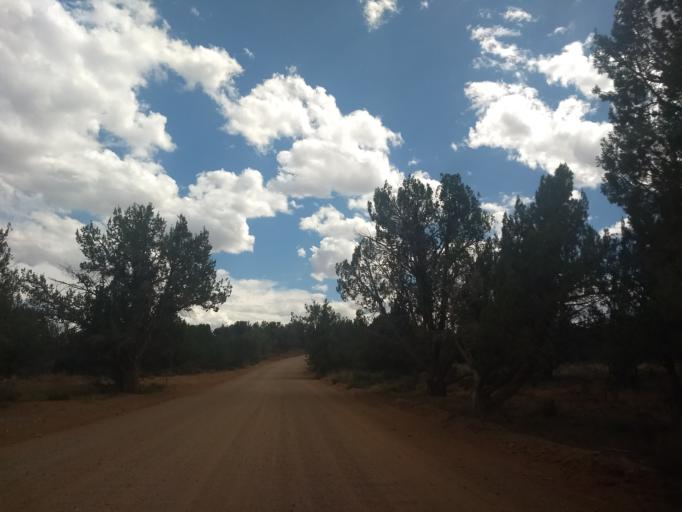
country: US
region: Utah
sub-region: Kane County
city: Kanab
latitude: 37.1503
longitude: -112.5449
